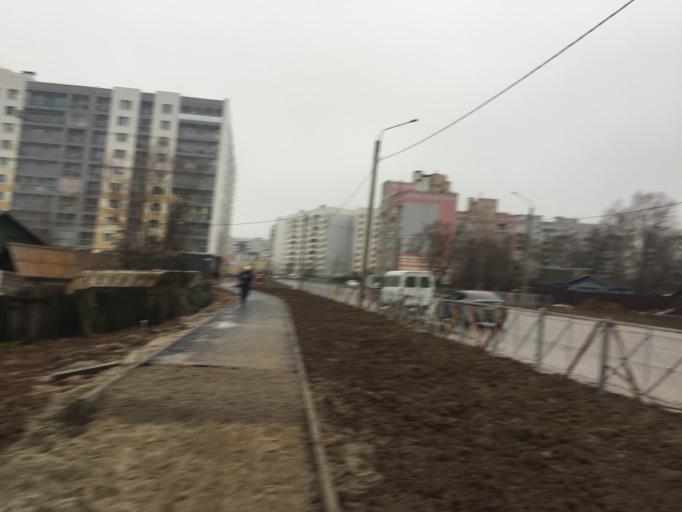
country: RU
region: Jaroslavl
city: Yaroslavl
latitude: 57.6975
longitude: 39.7854
